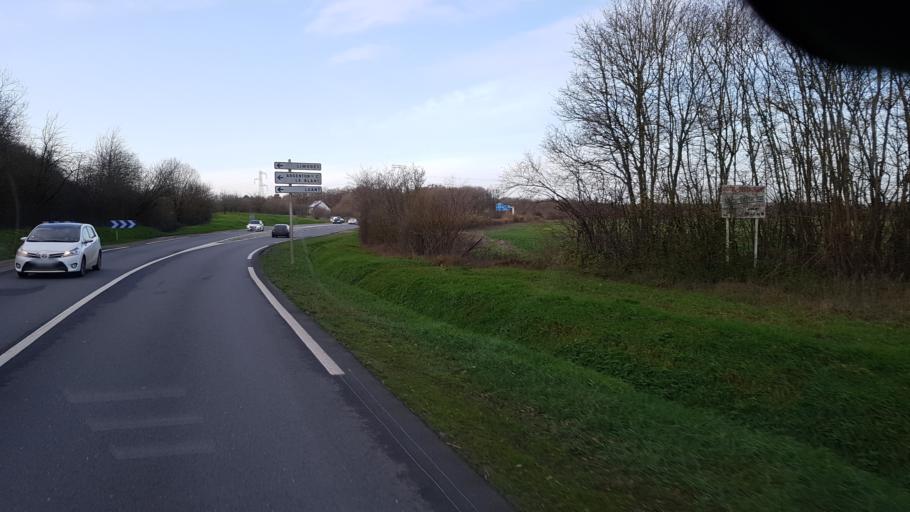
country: FR
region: Centre
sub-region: Departement de l'Indre
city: Saint-Maur
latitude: 46.7704
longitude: 1.6438
